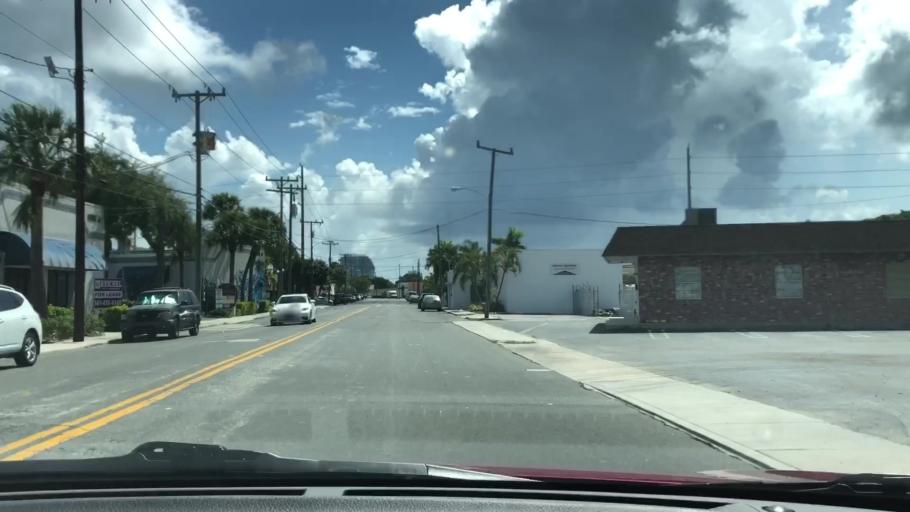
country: US
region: Florida
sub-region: Palm Beach County
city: West Palm Beach
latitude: 26.6994
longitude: -80.0674
